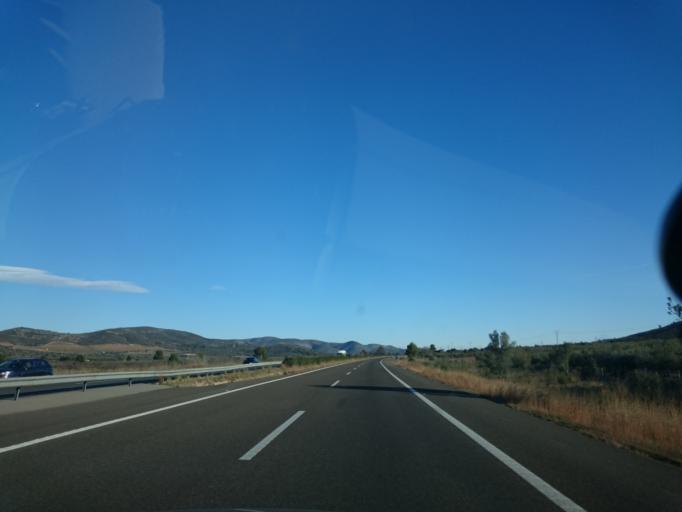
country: ES
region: Valencia
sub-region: Provincia de Castello
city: Alcala de Xivert
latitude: 40.3245
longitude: 0.2550
